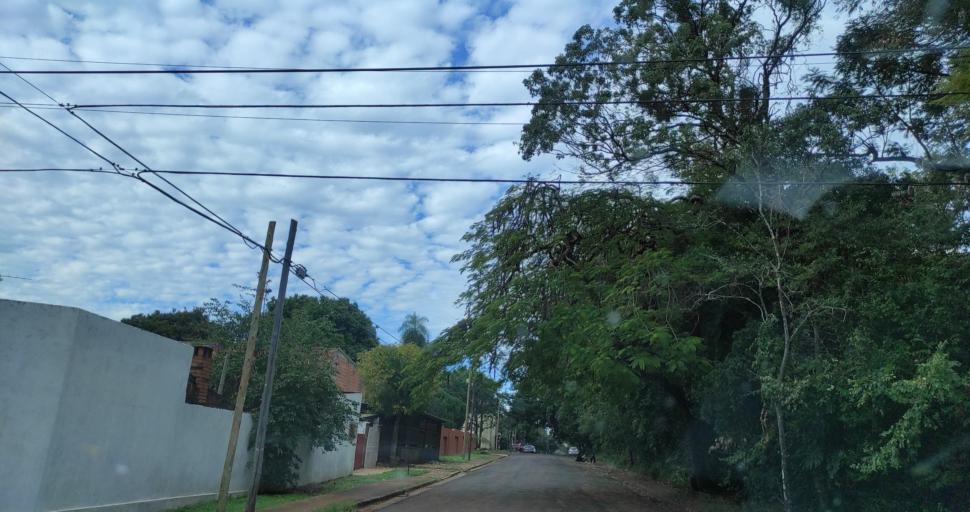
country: AR
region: Misiones
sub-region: Departamento de Capital
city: Posadas
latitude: -27.3654
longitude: -55.9228
